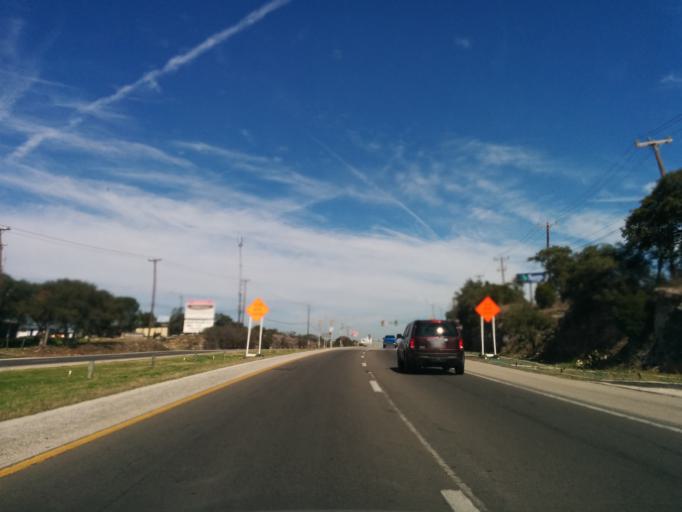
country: US
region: Texas
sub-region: Bexar County
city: Timberwood Park
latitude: 29.6579
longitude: -98.4500
